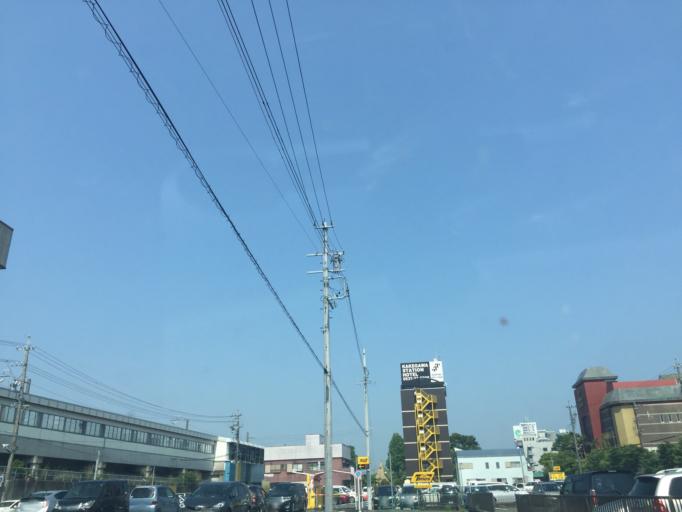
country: JP
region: Shizuoka
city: Kakegawa
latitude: 34.7683
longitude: 138.0127
